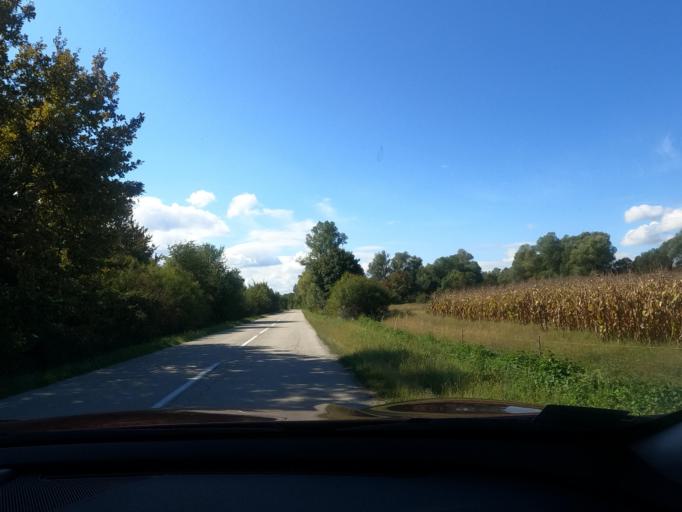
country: BA
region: Federation of Bosnia and Herzegovina
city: Vrnograc
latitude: 45.2518
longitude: 15.9439
